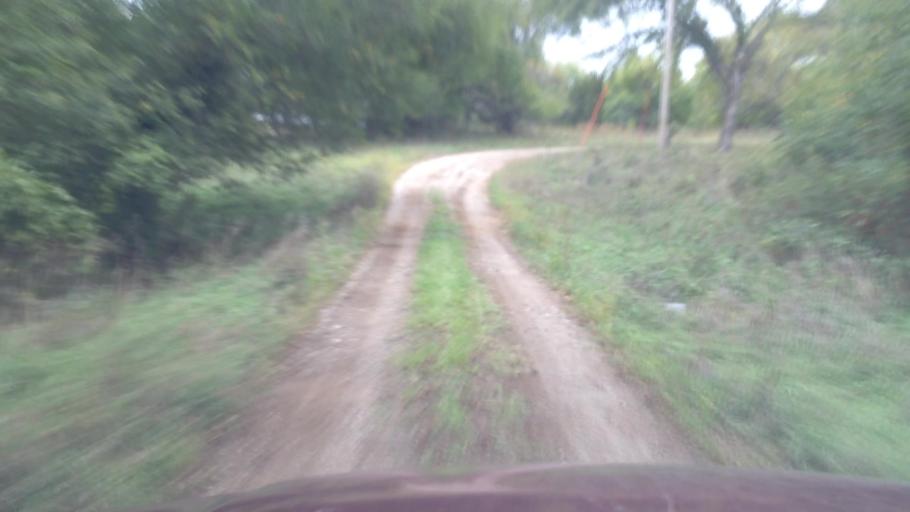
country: US
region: Kansas
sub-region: Jefferson County
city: Oskaloosa
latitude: 39.1233
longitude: -95.4793
